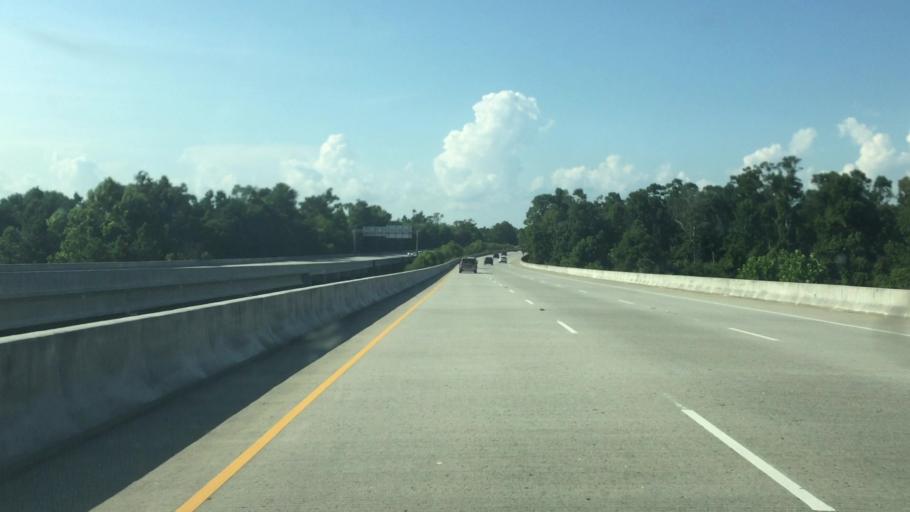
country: US
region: South Carolina
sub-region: Horry County
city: North Myrtle Beach
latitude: 33.7931
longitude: -78.7780
